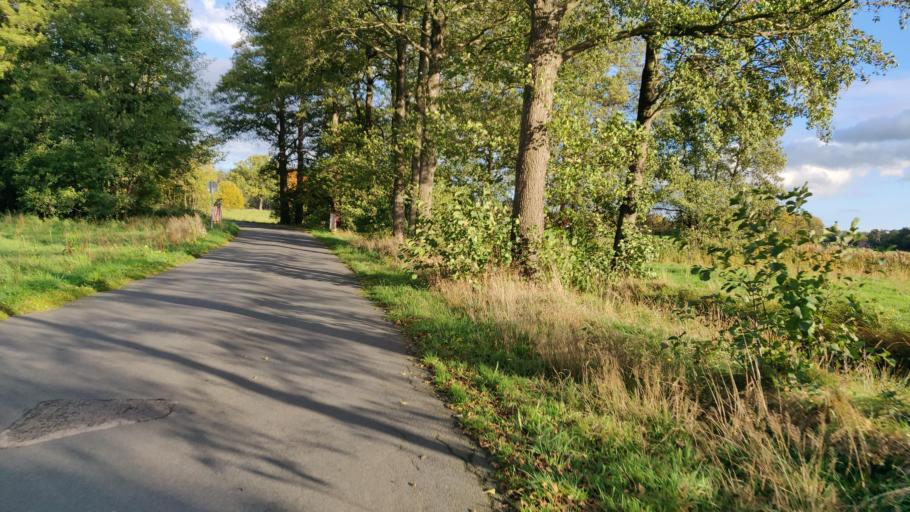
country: DE
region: Brandenburg
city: Ortrand
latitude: 51.3688
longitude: 13.7798
